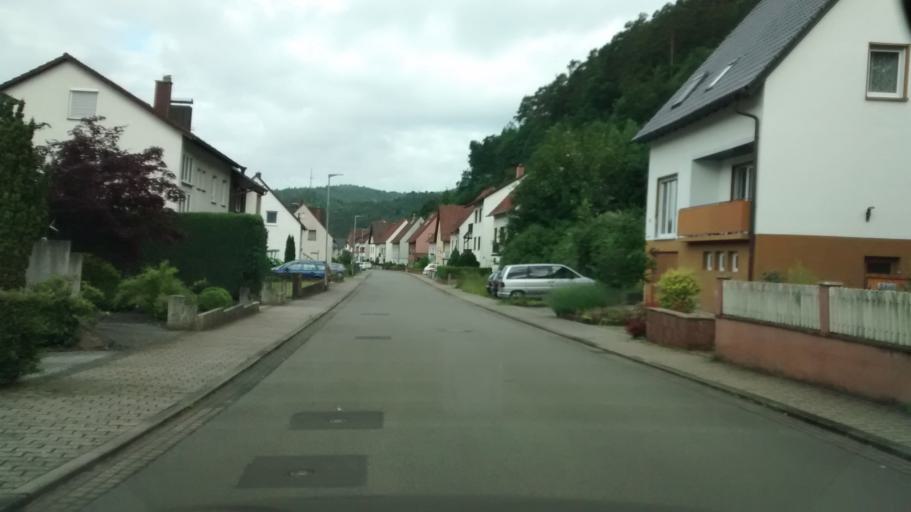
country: DE
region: Rheinland-Pfalz
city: Dahn
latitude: 49.1583
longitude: 7.7805
